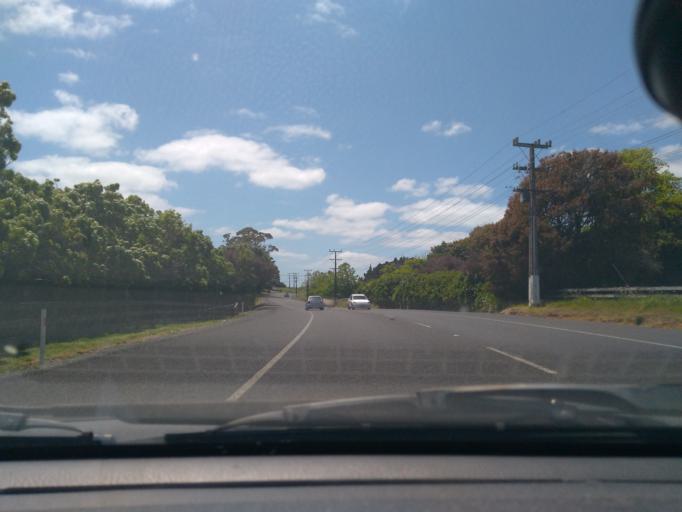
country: NZ
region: Auckland
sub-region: Auckland
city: Pakuranga
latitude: -36.9051
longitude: 175.0069
